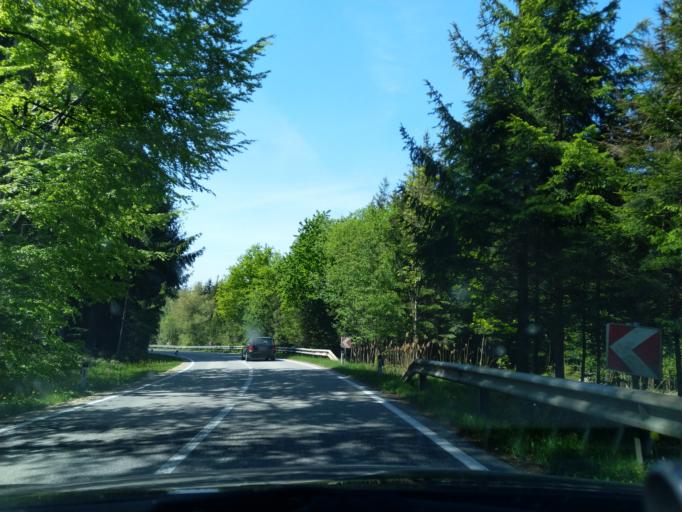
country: AT
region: Upper Austria
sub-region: Politischer Bezirk Ried im Innkreis
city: Ried im Innkreis
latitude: 48.2772
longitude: 13.3987
